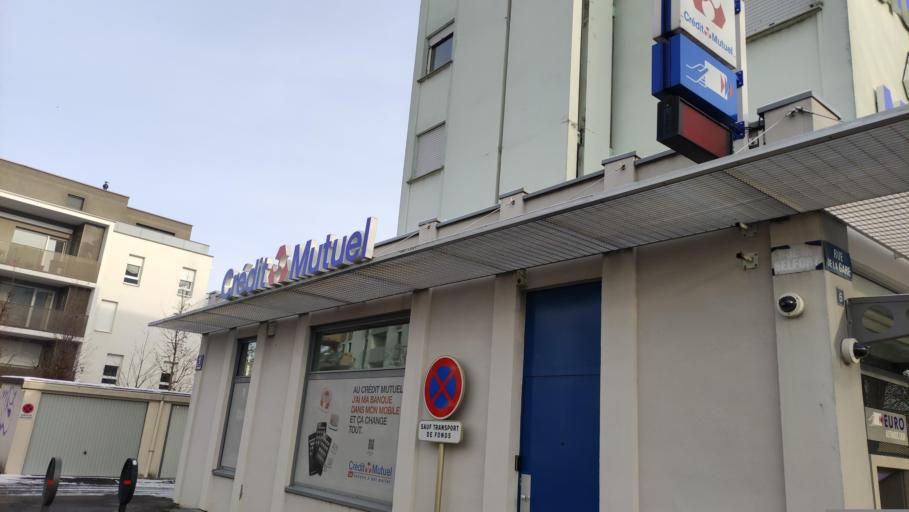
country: FR
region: Alsace
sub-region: Departement du Haut-Rhin
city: Huningue
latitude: 47.5941
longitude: 7.5815
